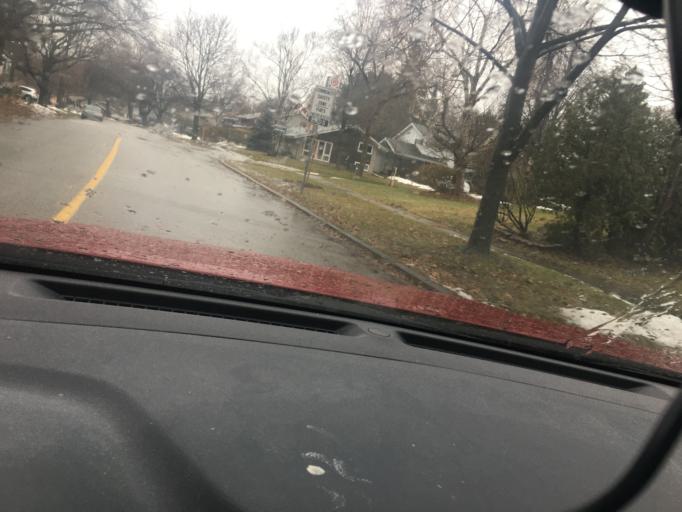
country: CA
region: Ontario
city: Scarborough
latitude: 43.7640
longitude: -79.2671
